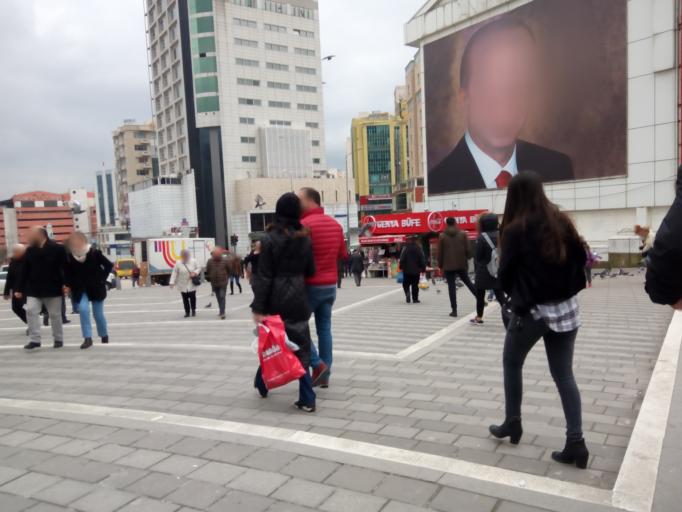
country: TR
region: Bursa
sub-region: Osmangazi
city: Bursa
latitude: 40.1881
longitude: 29.0610
